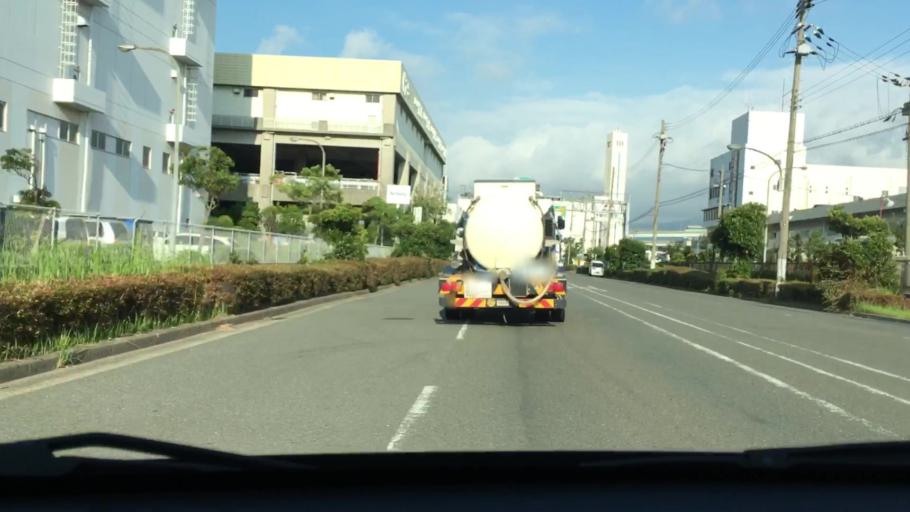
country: JP
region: Hyogo
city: Ashiya
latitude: 34.6944
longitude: 135.2797
